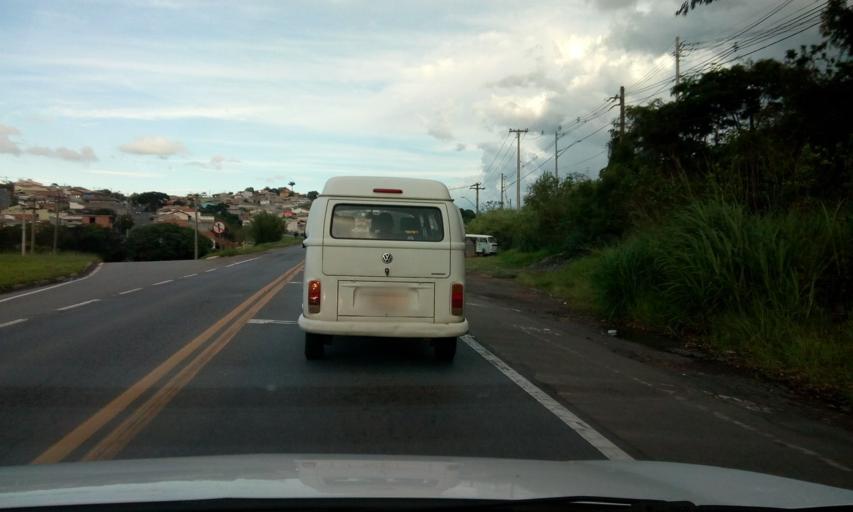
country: BR
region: Sao Paulo
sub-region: Itatiba
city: Itatiba
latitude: -23.0146
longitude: -46.8281
